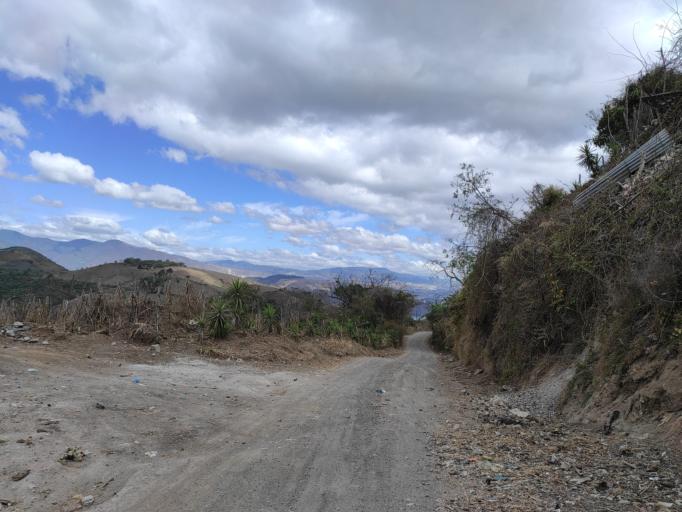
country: GT
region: Guatemala
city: Villa Canales
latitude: 14.4414
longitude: -90.5713
